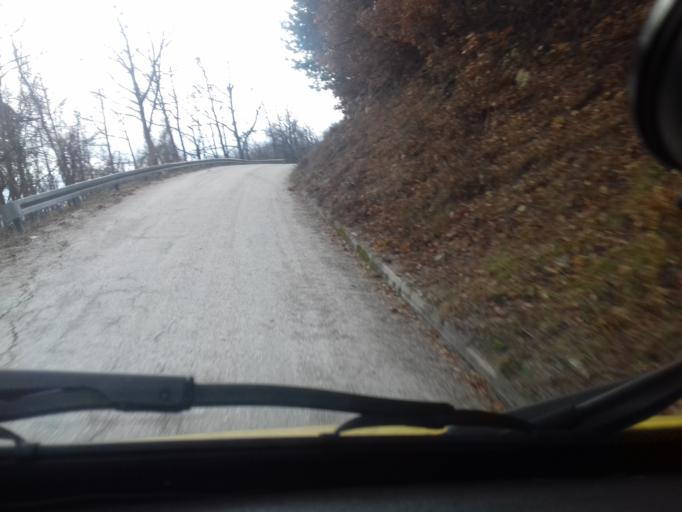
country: BA
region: Federation of Bosnia and Herzegovina
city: Zenica
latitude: 44.2276
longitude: 17.9620
